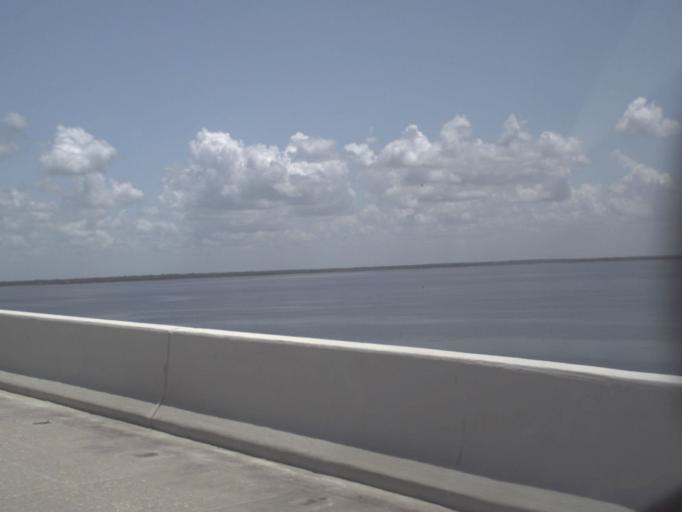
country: US
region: Florida
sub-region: Walton County
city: Seaside
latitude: 30.3960
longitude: -86.1705
